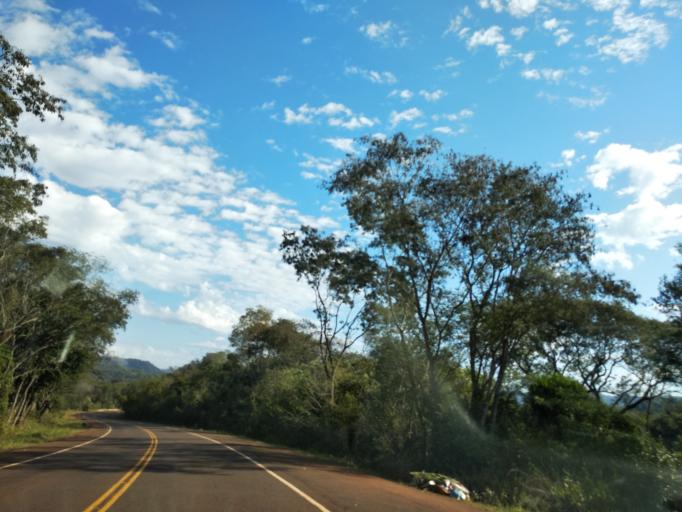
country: AR
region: Misiones
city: Aristobulo del Valle
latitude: -27.0993
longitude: -54.9599
